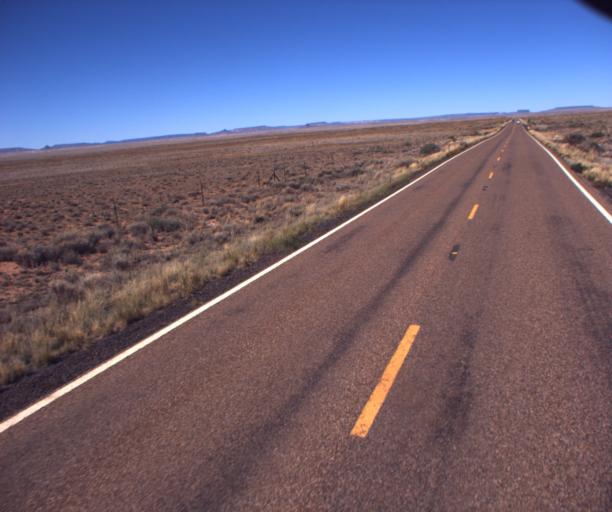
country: US
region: Arizona
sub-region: Navajo County
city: Holbrook
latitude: 35.0177
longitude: -110.0901
